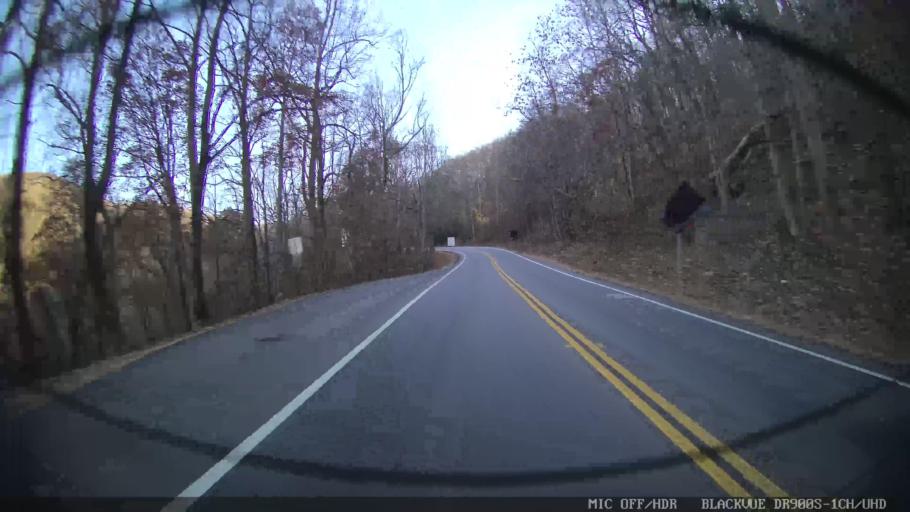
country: US
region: Georgia
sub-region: Union County
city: Blairsville
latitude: 34.7382
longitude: -83.9186
